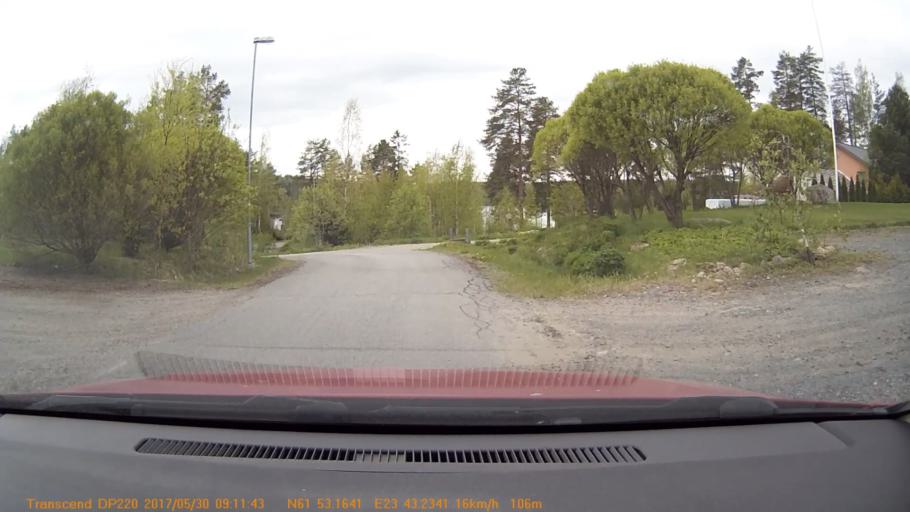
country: FI
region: Pirkanmaa
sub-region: Tampere
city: Kuru
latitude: 61.8861
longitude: 23.7205
